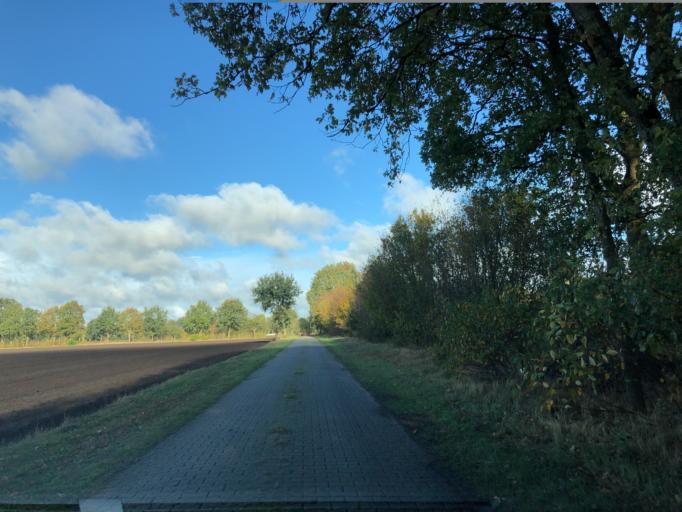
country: DE
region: Lower Saxony
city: Neulehe
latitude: 53.0246
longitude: 7.3670
